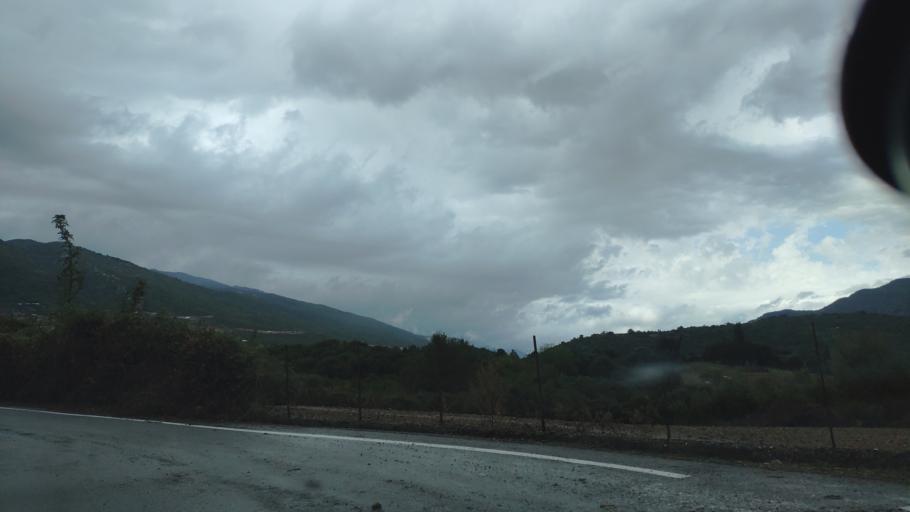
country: GR
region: Central Greece
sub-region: Nomos Evrytanias
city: Kerasochori
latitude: 39.1036
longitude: 21.4278
